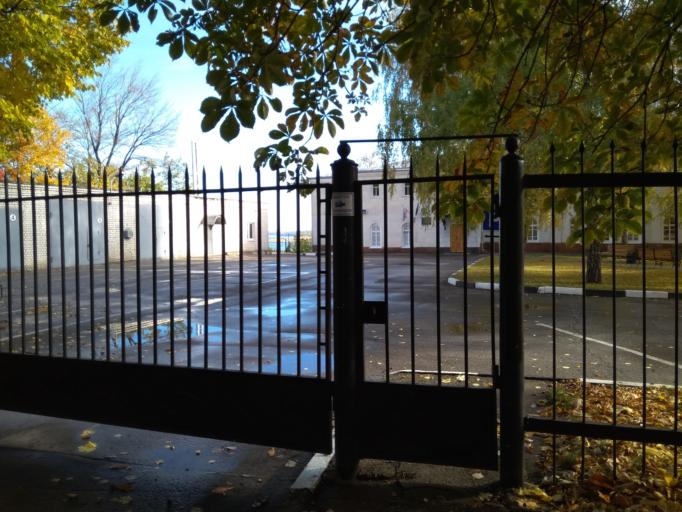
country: RU
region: Ulyanovsk
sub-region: Ulyanovskiy Rayon
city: Ulyanovsk
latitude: 54.3285
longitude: 48.4080
